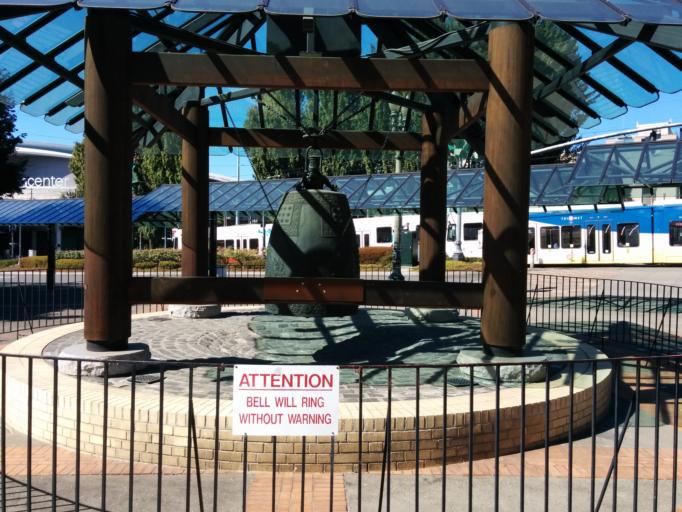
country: US
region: Oregon
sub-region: Multnomah County
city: Portland
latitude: 45.5298
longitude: -122.6637
